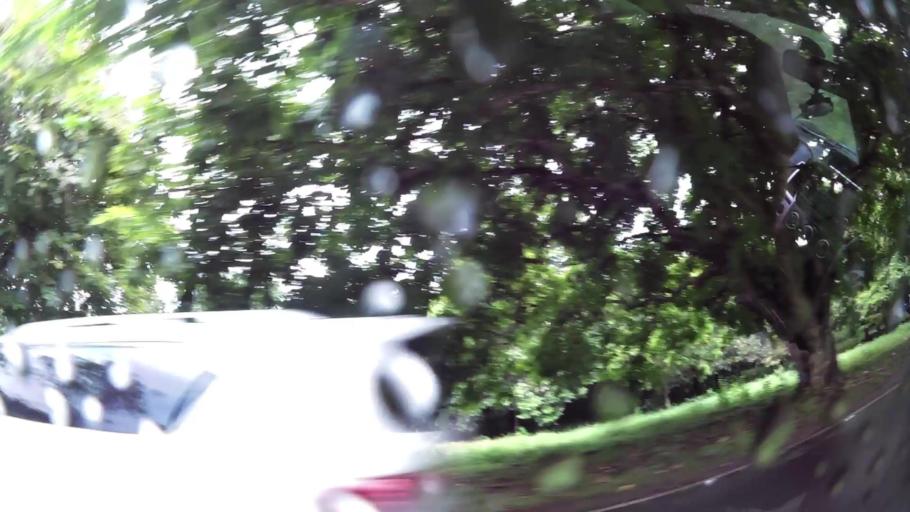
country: PA
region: Panama
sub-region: Distrito de Panama
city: Ancon
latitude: 8.9882
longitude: -79.5560
